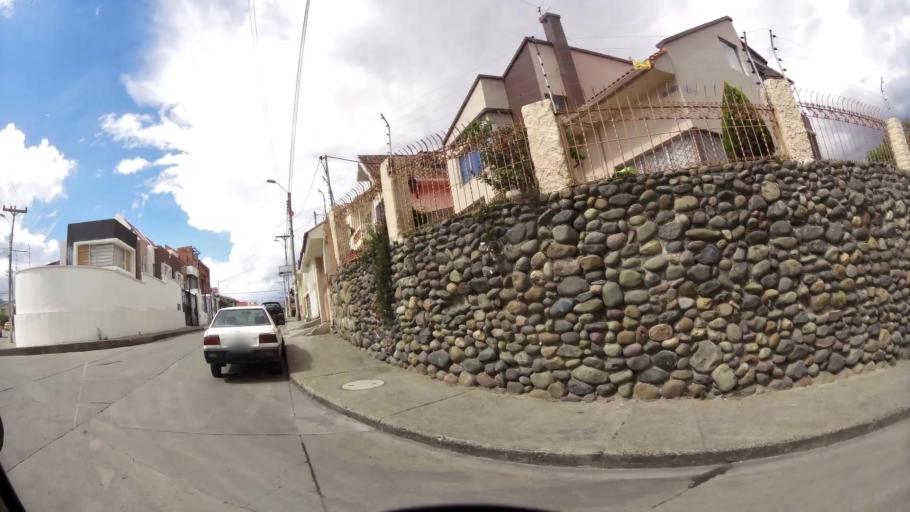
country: EC
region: Azuay
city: Cuenca
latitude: -2.8820
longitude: -78.9791
